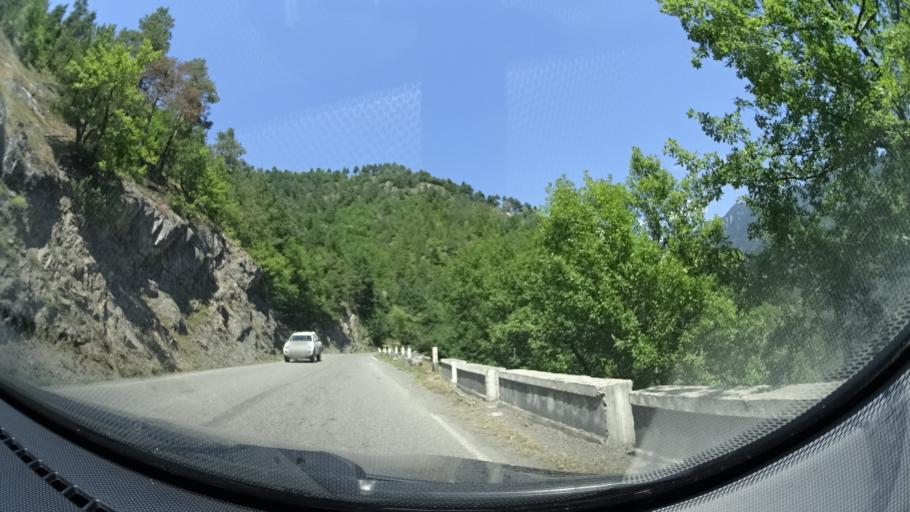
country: GE
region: Ajaria
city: Khulo
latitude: 41.6281
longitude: 42.2878
